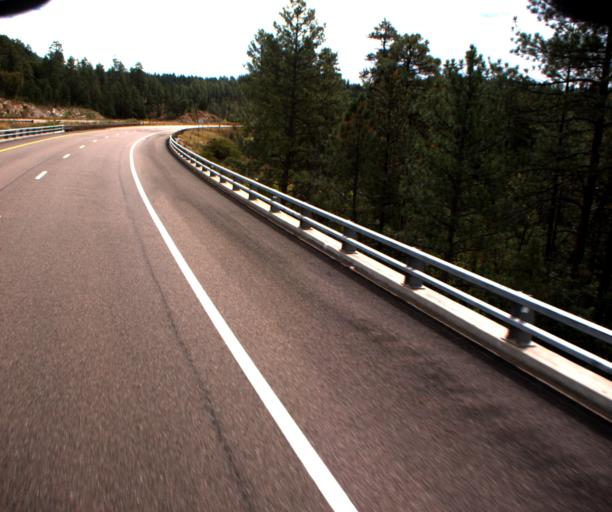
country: US
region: Arizona
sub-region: Gila County
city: Star Valley
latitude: 34.3140
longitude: -111.0316
